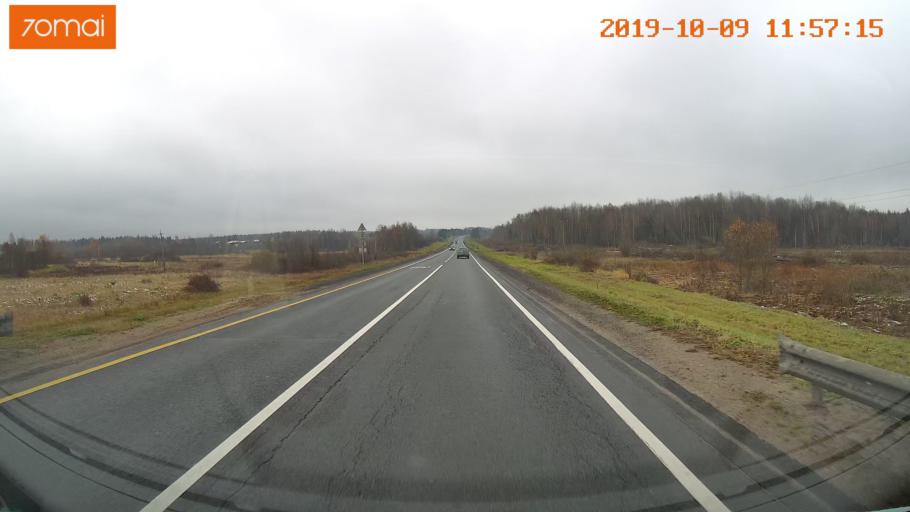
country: RU
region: Vologda
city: Gryazovets
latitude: 58.7348
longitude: 40.2915
